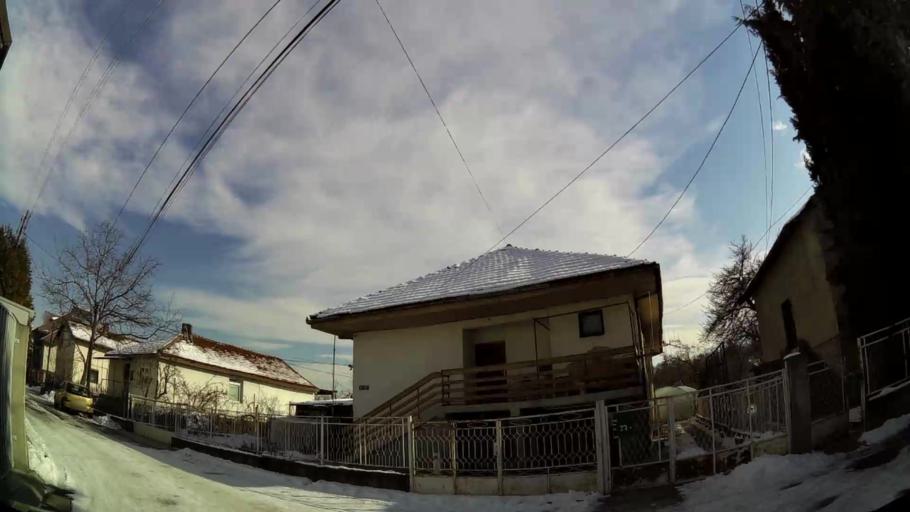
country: MK
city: Krushopek
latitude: 41.9985
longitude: 21.3716
